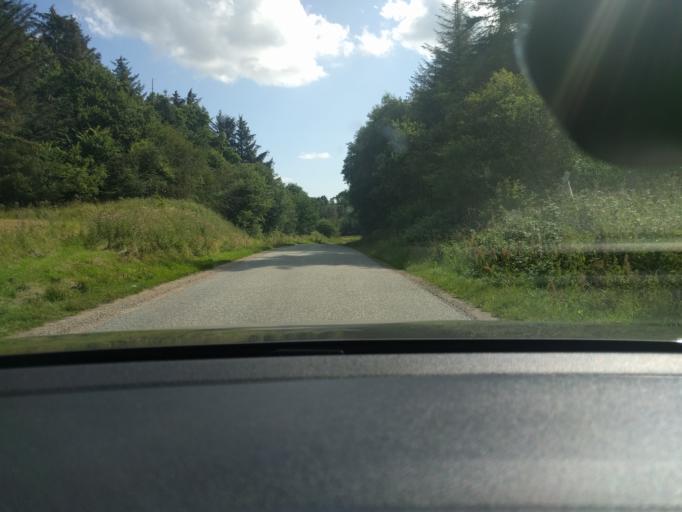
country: DK
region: Central Jutland
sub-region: Viborg Kommune
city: Viborg
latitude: 56.5234
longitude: 9.4014
